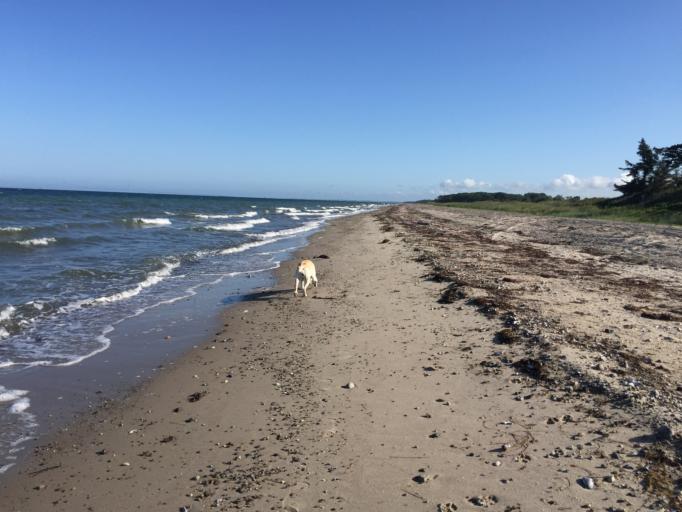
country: DK
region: Zealand
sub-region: Slagelse Kommune
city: Korsor
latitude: 55.2128
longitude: 11.1723
